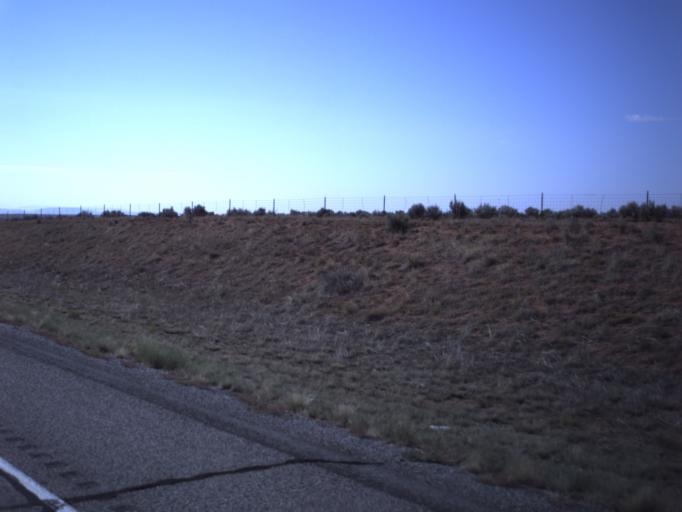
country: US
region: Utah
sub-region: San Juan County
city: Blanding
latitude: 37.4978
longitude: -109.4838
